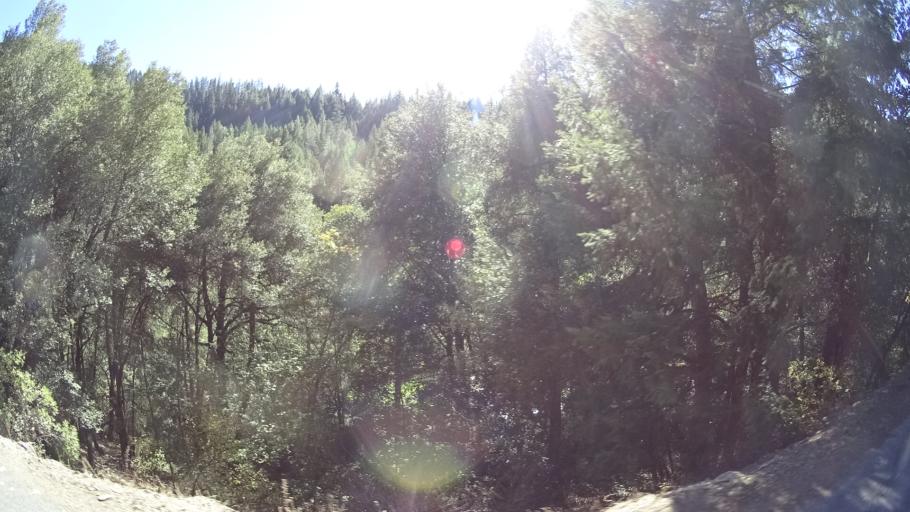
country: US
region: California
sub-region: Siskiyou County
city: Happy Camp
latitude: 41.2959
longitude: -123.1162
